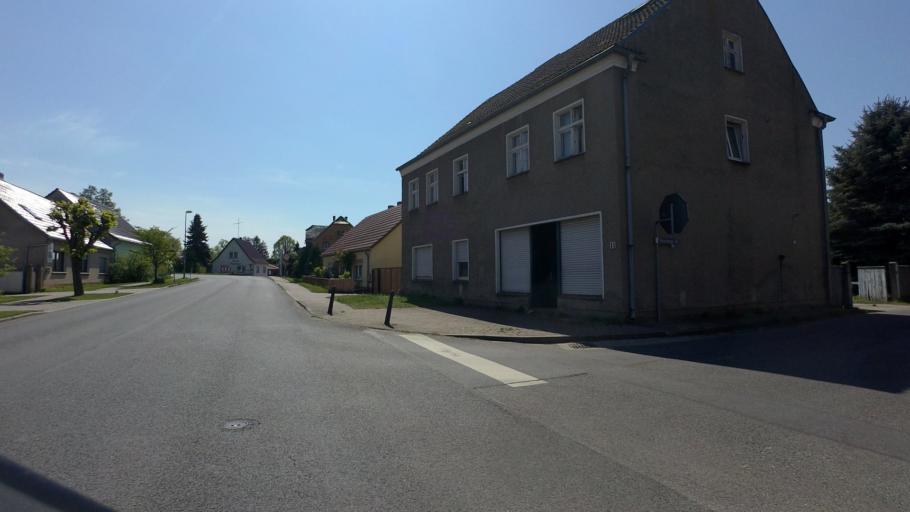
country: DE
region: Brandenburg
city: Schlepzig
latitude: 52.0796
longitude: 13.8780
